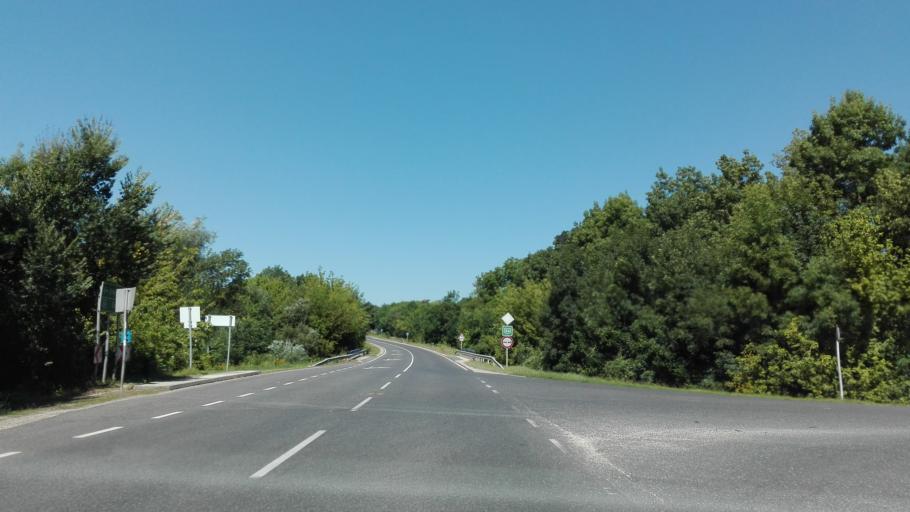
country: HU
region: Fejer
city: Deg
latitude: 46.8595
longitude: 18.4276
